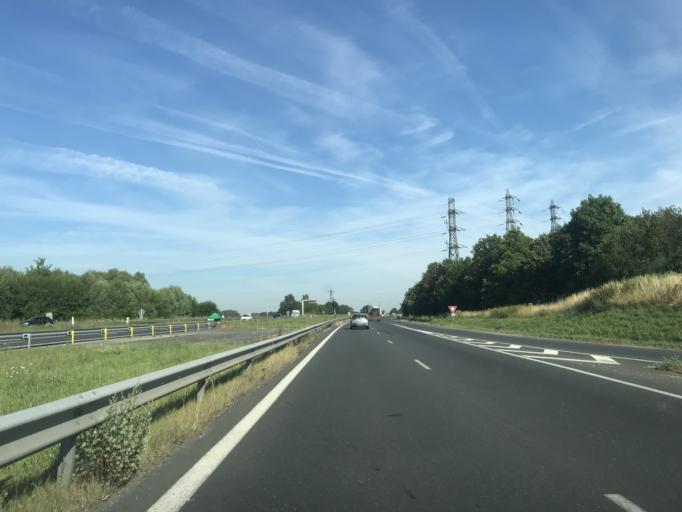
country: FR
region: Haute-Normandie
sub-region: Departement de la Seine-Maritime
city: Maromme
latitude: 49.4812
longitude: 1.0100
